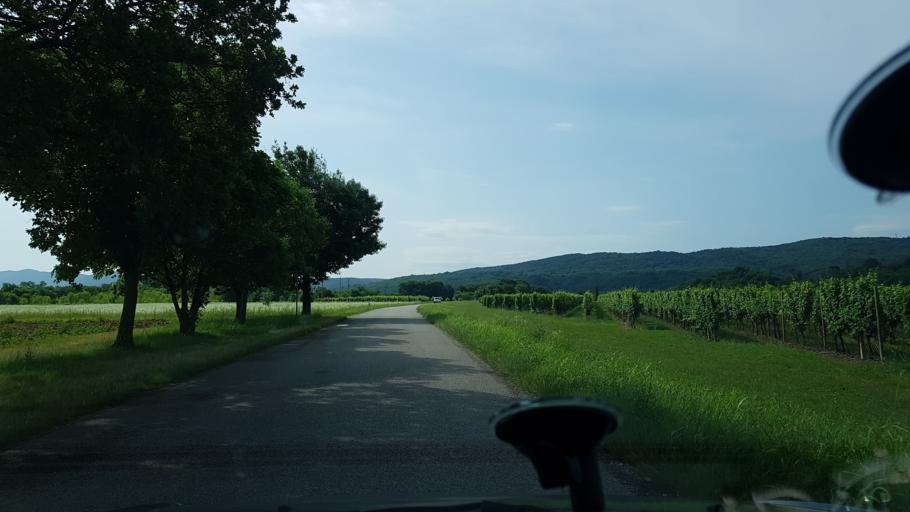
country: IT
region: Friuli Venezia Giulia
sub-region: Provincia di Gorizia
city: Mossa
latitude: 45.9150
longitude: 13.5460
